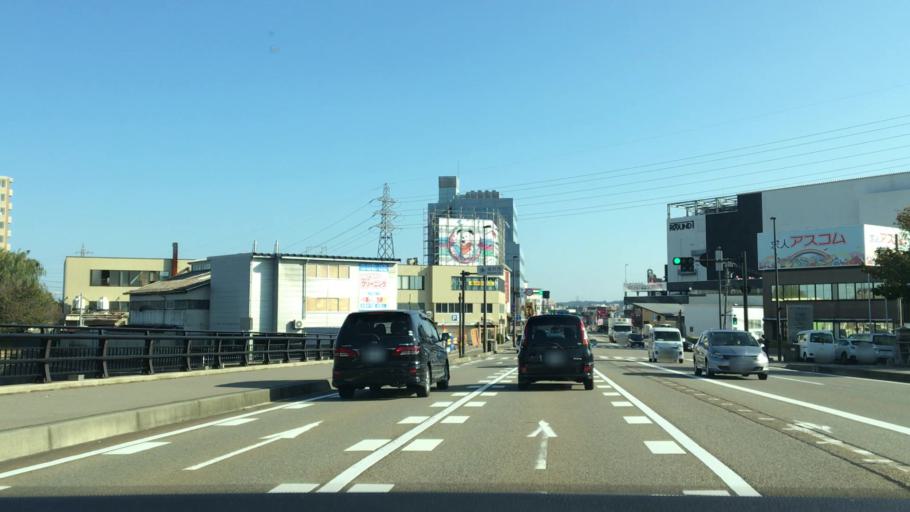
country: JP
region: Ishikawa
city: Nonoichi
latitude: 36.5411
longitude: 136.6236
